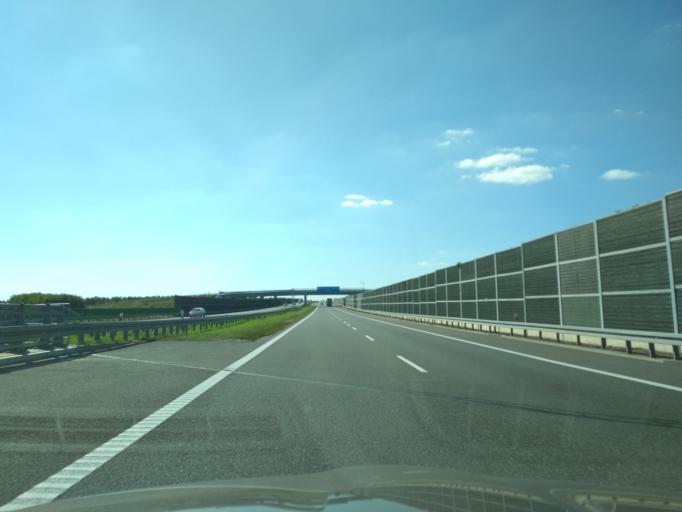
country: PL
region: Subcarpathian Voivodeship
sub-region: Powiat rzeszowski
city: Trzebownisko
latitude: 50.0972
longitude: 22.0267
